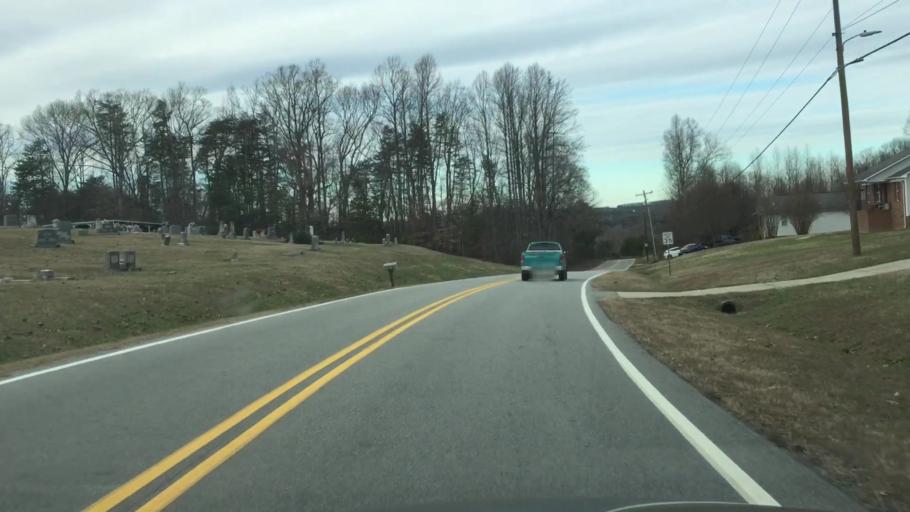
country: US
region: North Carolina
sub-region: Rockingham County
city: Reidsville
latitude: 36.3894
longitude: -79.6551
